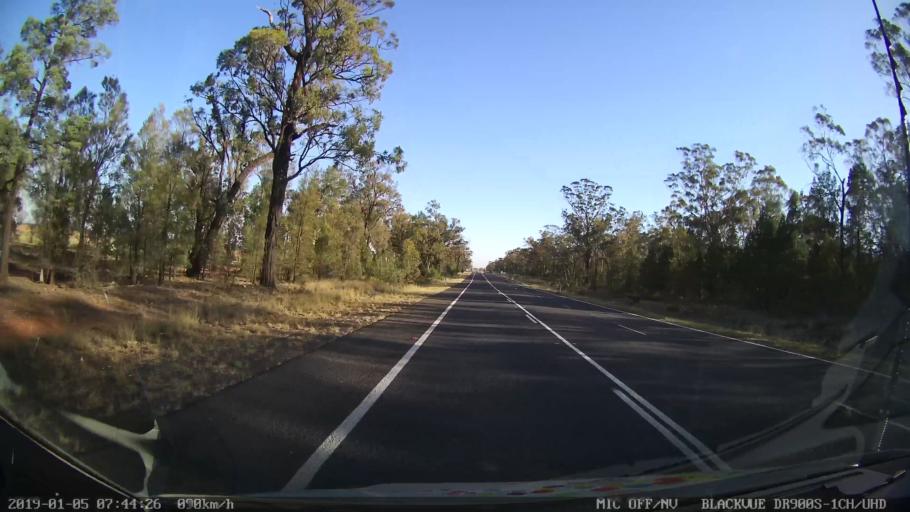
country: AU
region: New South Wales
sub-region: Gilgandra
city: Gilgandra
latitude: -31.8725
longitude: 148.6395
